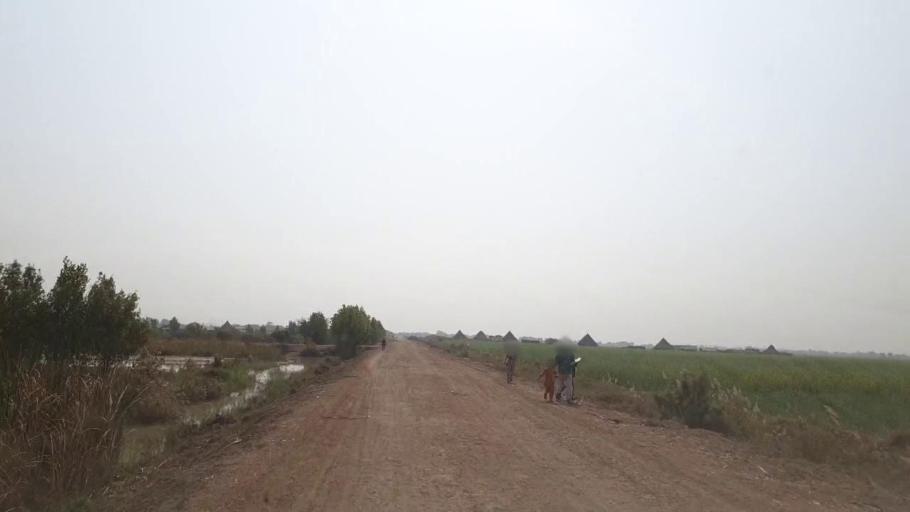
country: PK
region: Sindh
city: Mirpur Khas
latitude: 25.5437
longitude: 69.0604
